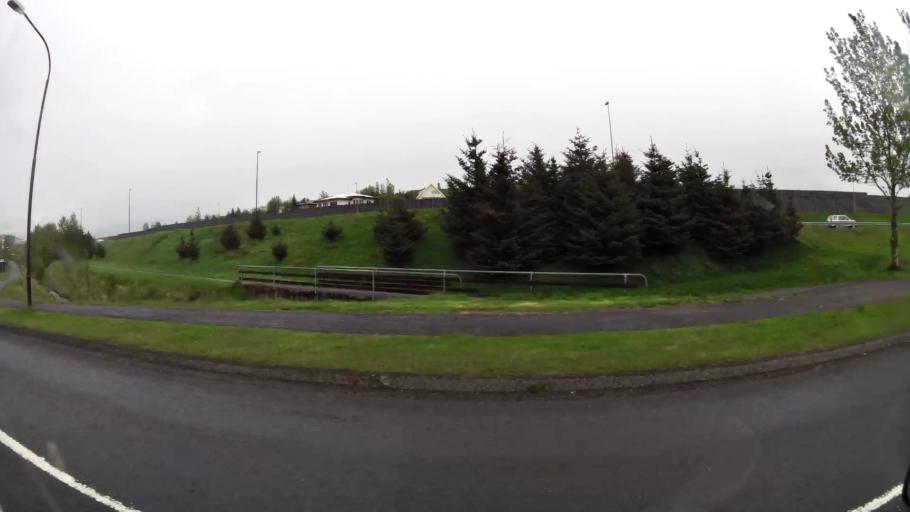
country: IS
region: Capital Region
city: Gardabaer
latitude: 64.0898
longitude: -21.8932
